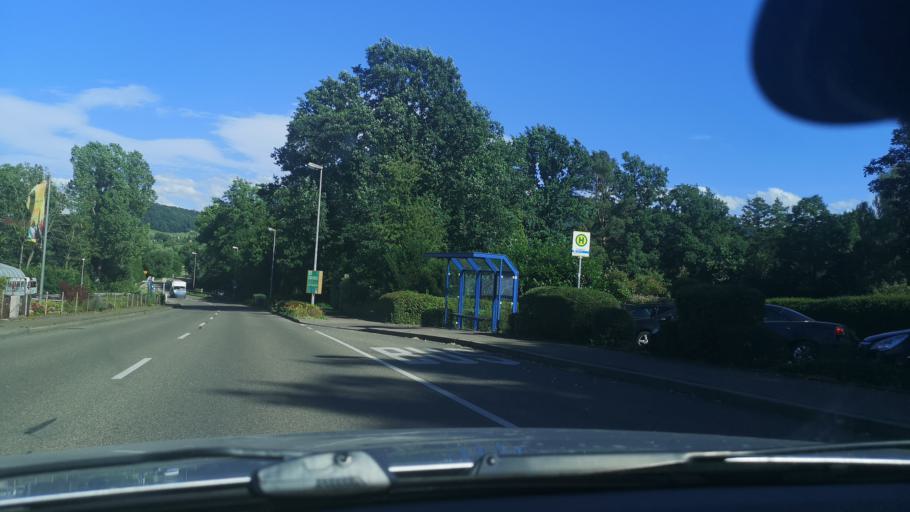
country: DE
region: Baden-Wuerttemberg
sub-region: Regierungsbezirk Stuttgart
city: Heiningen
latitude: 48.6578
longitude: 9.6518
